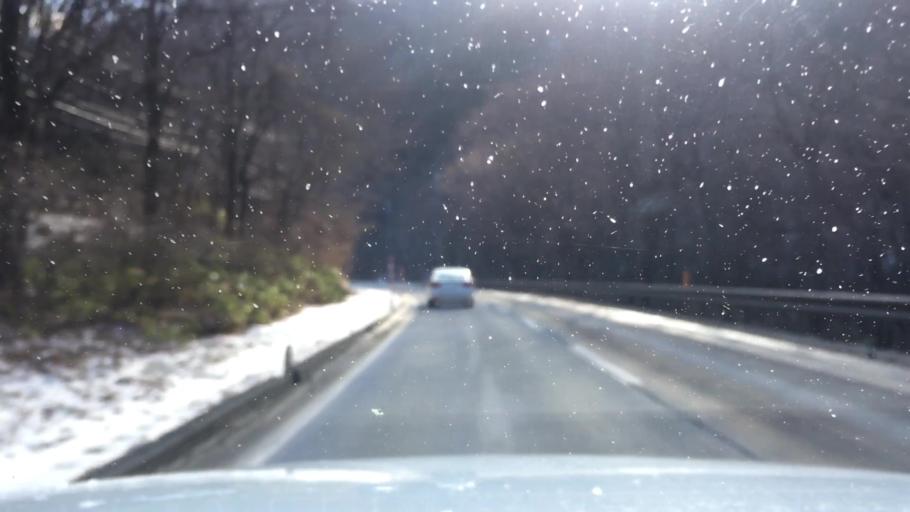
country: JP
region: Iwate
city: Tono
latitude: 39.6176
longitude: 141.4977
